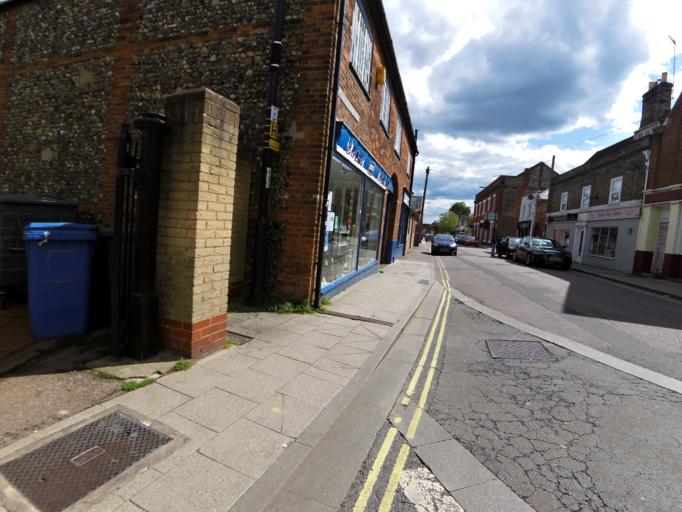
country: GB
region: England
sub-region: Suffolk
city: Bury St Edmunds
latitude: 52.2447
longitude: 0.7111
